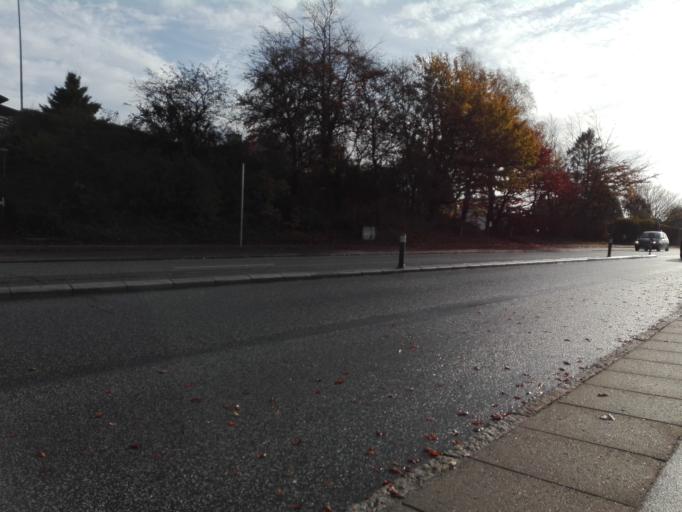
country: DK
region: Central Jutland
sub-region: Arhus Kommune
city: Beder
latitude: 56.1014
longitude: 10.2077
